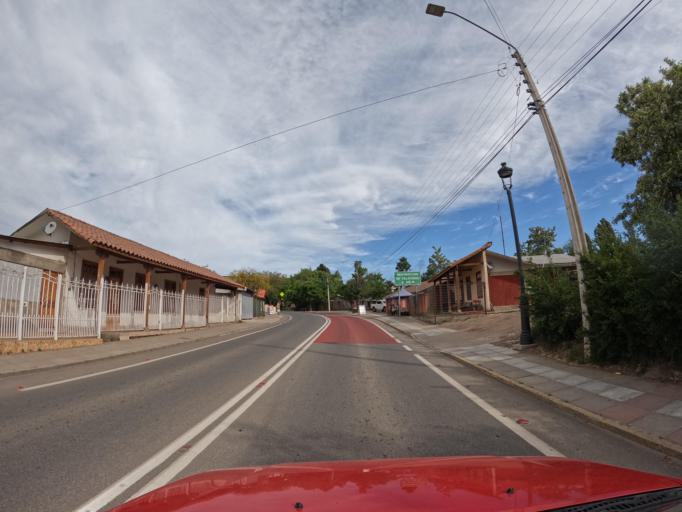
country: CL
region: Maule
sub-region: Provincia de Talca
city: Talca
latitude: -35.3952
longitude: -71.8003
